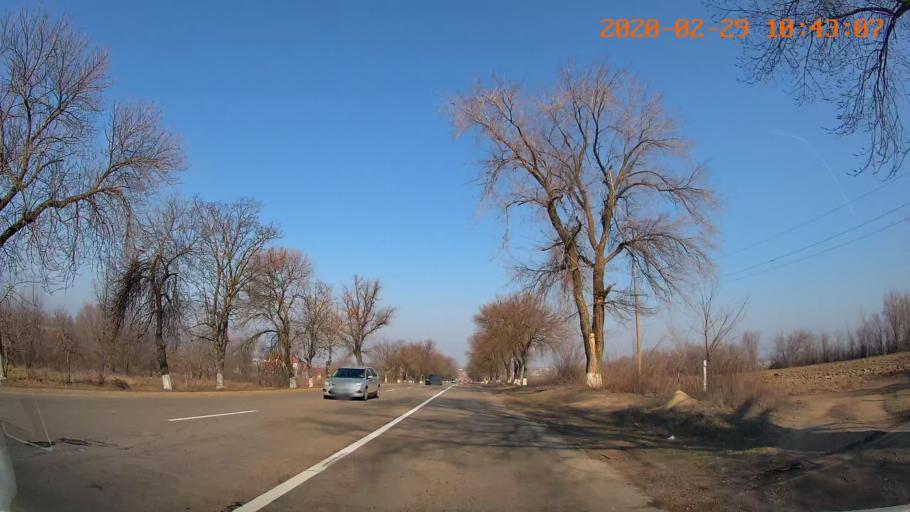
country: MD
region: Telenesti
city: Grigoriopol
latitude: 47.0579
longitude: 29.4049
